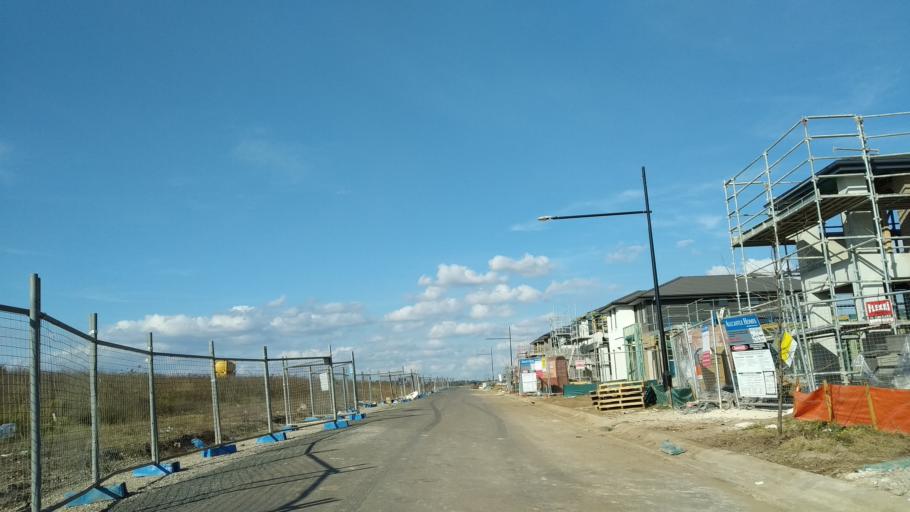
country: AU
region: New South Wales
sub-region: Blacktown
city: Blackett
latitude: -33.6870
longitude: 150.8080
